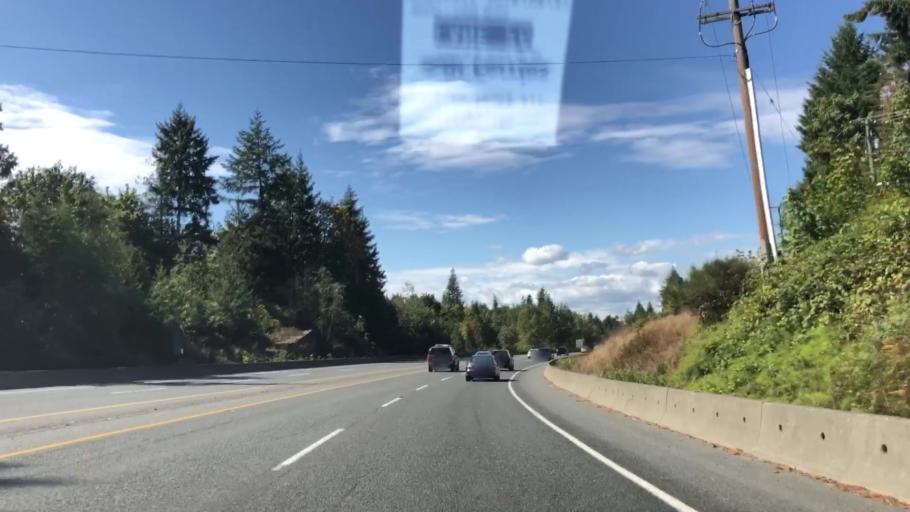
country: CA
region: British Columbia
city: Nanaimo
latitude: 49.1173
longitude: -123.8667
